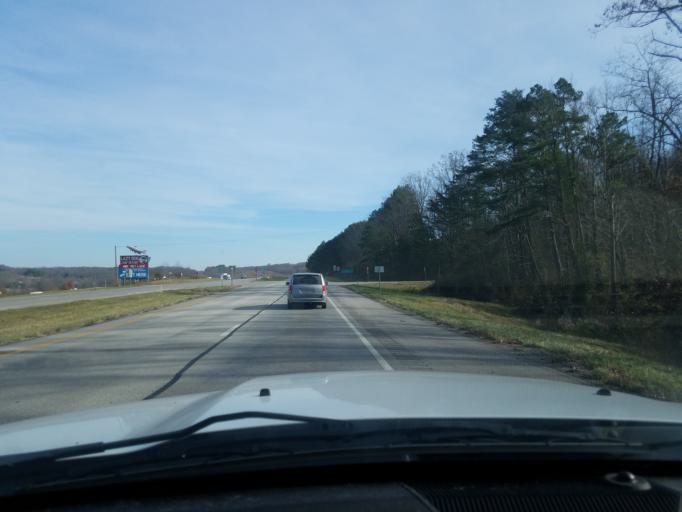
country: US
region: Ohio
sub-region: Jackson County
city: Wellston
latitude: 39.0738
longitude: -82.5495
